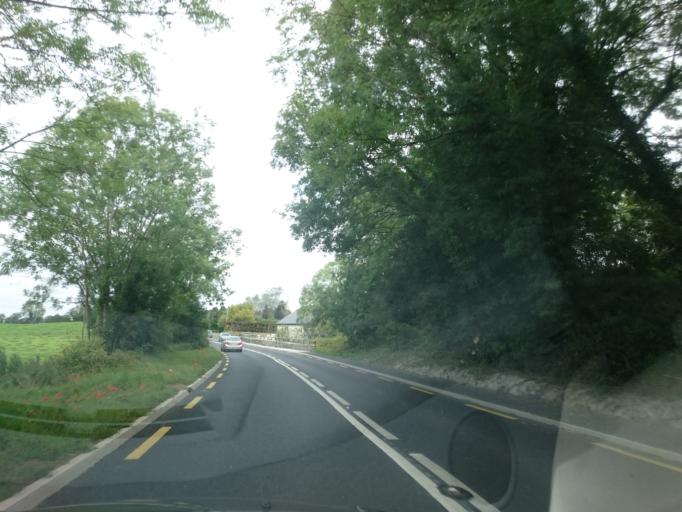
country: IE
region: Leinster
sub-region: Kilkenny
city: Kilkenny
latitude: 52.6800
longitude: -7.2538
